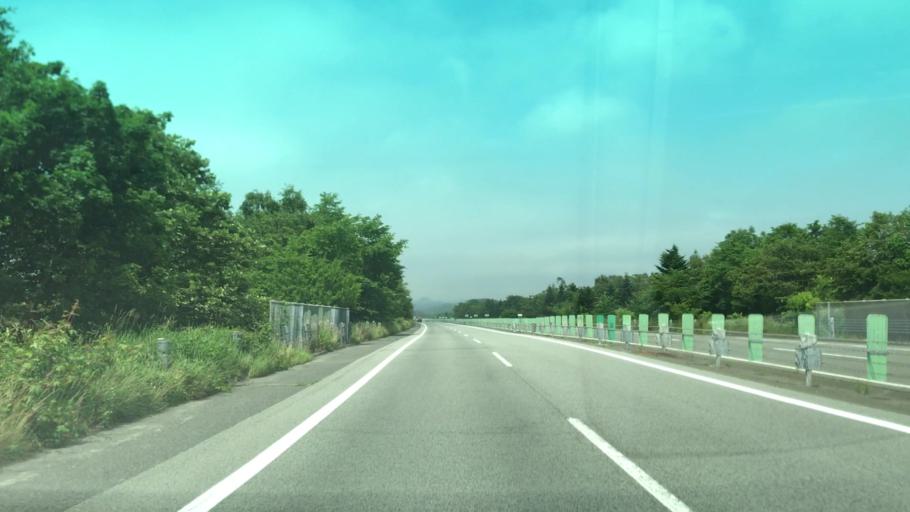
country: JP
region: Hokkaido
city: Shiraoi
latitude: 42.5142
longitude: 141.2698
